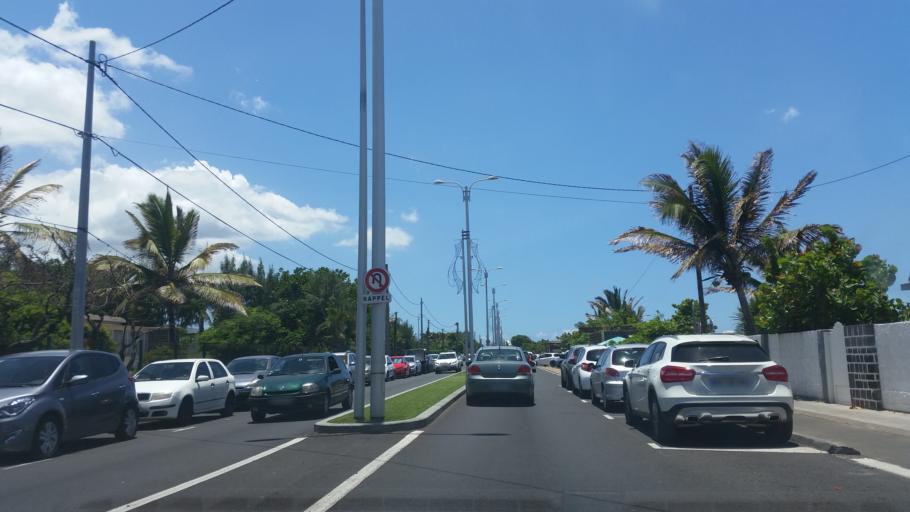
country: RE
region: Reunion
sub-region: Reunion
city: Saint-Pierre
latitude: -21.3422
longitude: 55.4646
